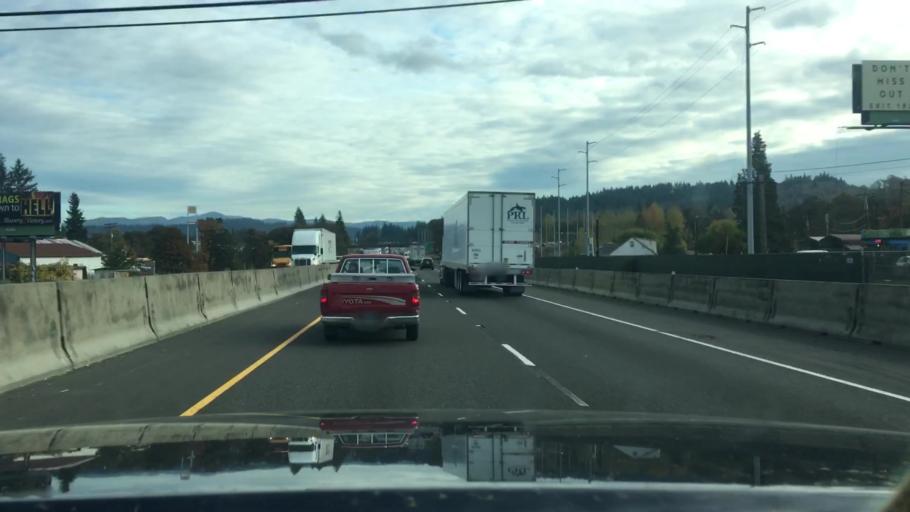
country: US
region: Oregon
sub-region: Lane County
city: Springfield
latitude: 44.0181
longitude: -123.0254
